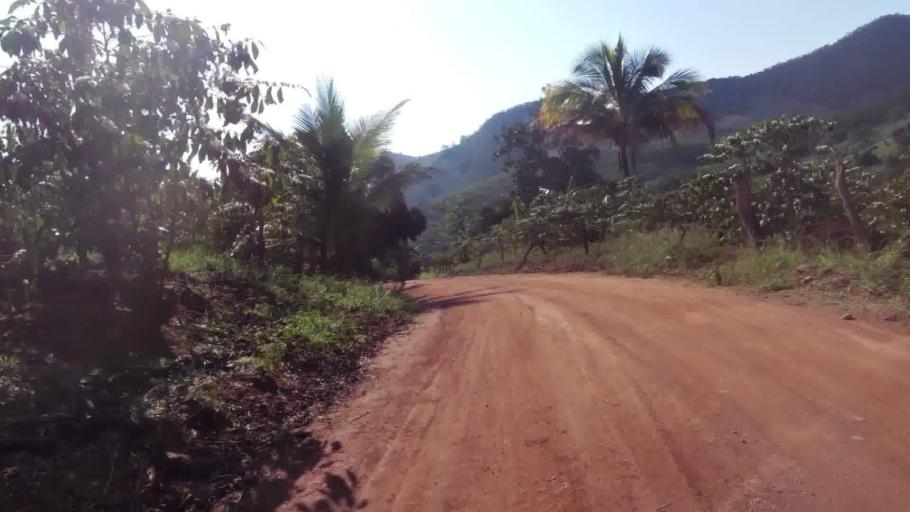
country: BR
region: Espirito Santo
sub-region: Alfredo Chaves
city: Alfredo Chaves
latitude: -20.6900
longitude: -40.7805
